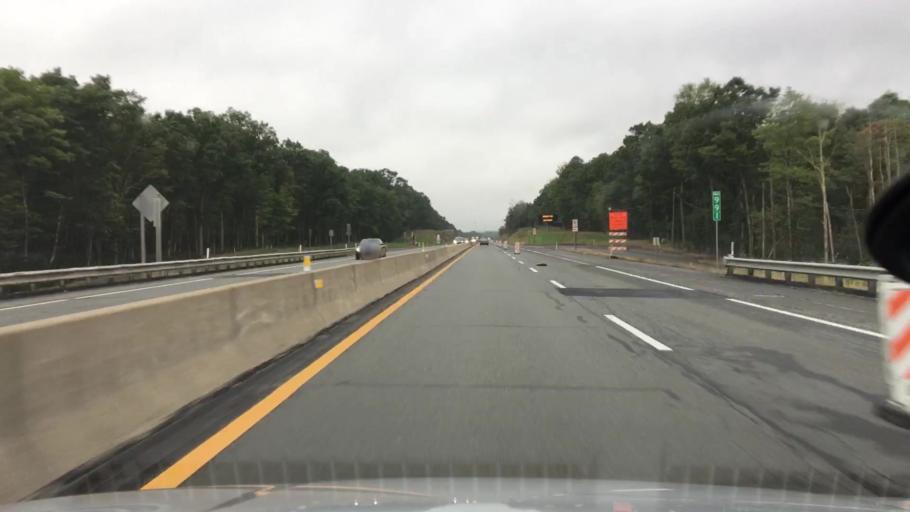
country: US
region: Pennsylvania
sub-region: Luzerne County
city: White Haven
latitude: 41.1156
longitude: -75.7623
